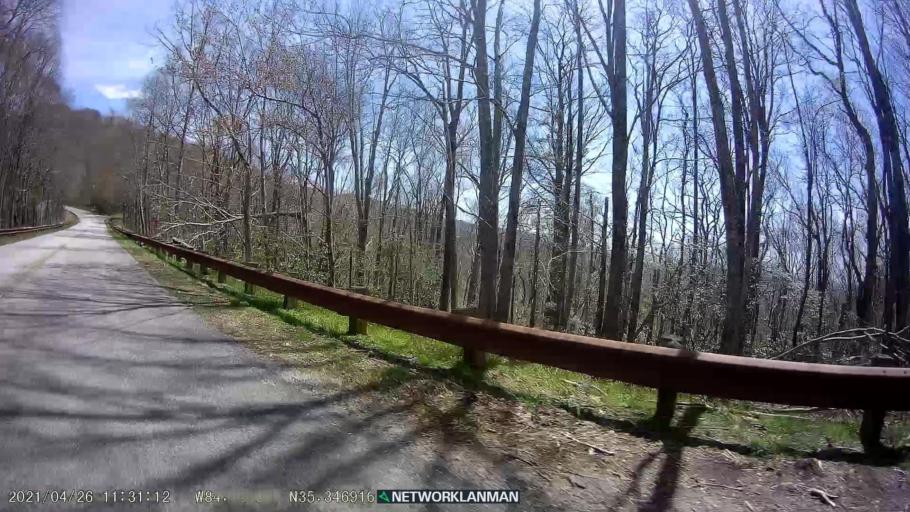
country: US
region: North Carolina
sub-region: Graham County
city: Robbinsville
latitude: 35.3469
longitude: -84.0557
